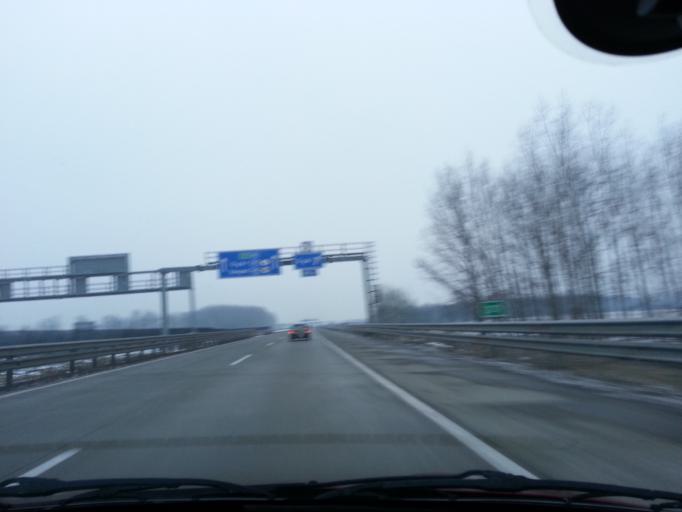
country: HU
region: Pest
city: Vecses
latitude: 47.3812
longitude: 19.2739
